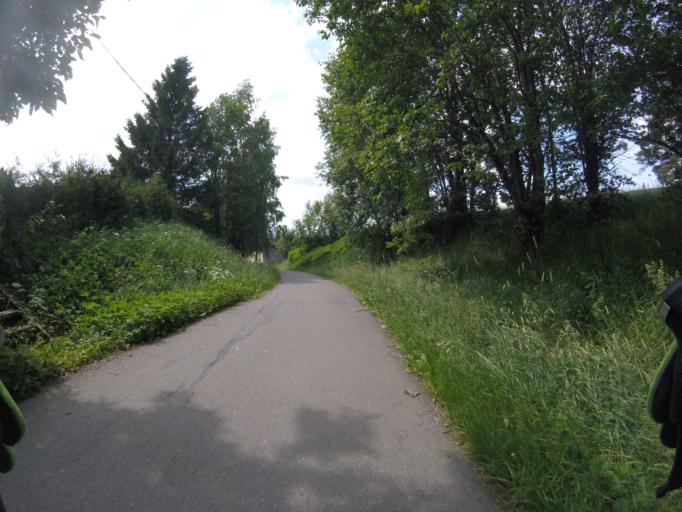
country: NO
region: Akershus
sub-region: Skedsmo
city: Lillestrom
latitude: 59.9732
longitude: 11.0556
